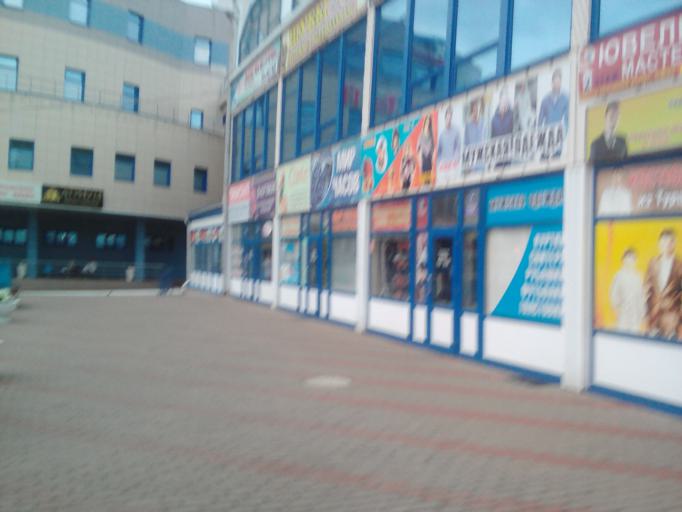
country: RU
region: Kursk
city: Kursk
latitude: 51.7287
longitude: 36.1835
